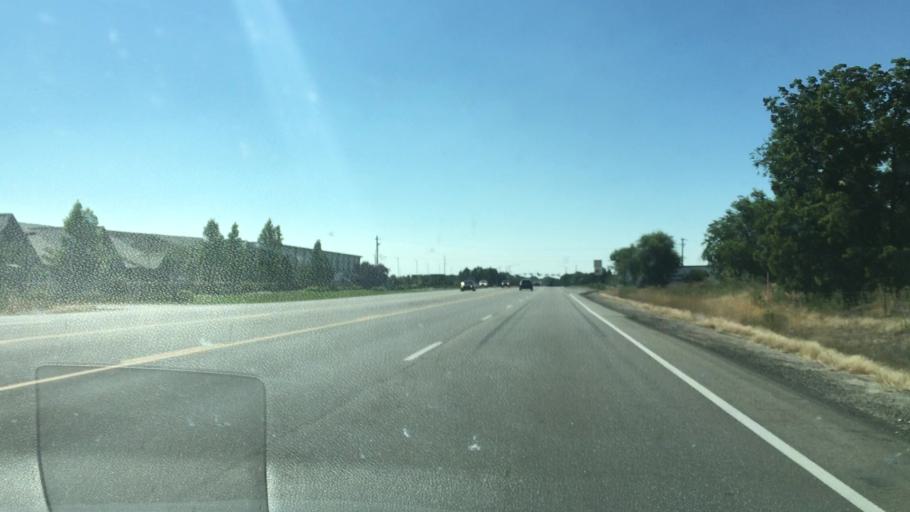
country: US
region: Idaho
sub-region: Ada County
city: Eagle
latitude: 43.6866
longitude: -116.3284
